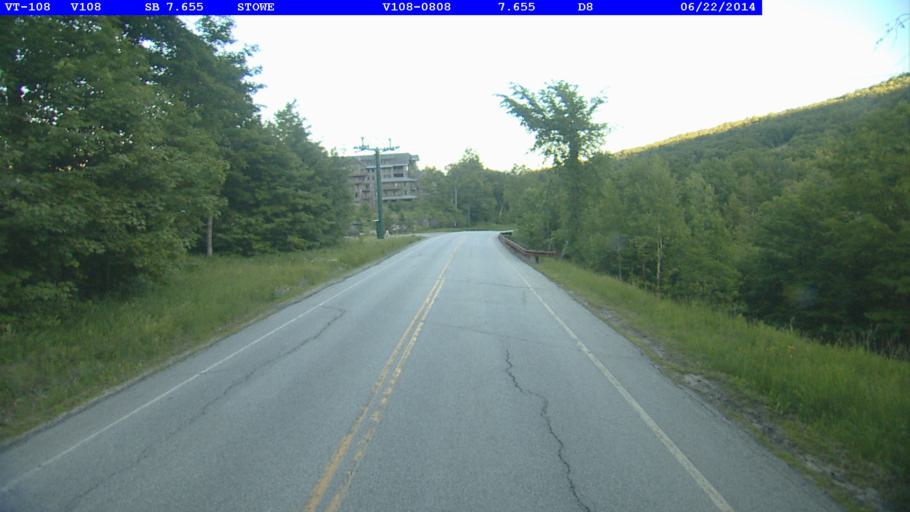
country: US
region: Vermont
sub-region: Lamoille County
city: Johnson
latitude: 44.5311
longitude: -72.7840
